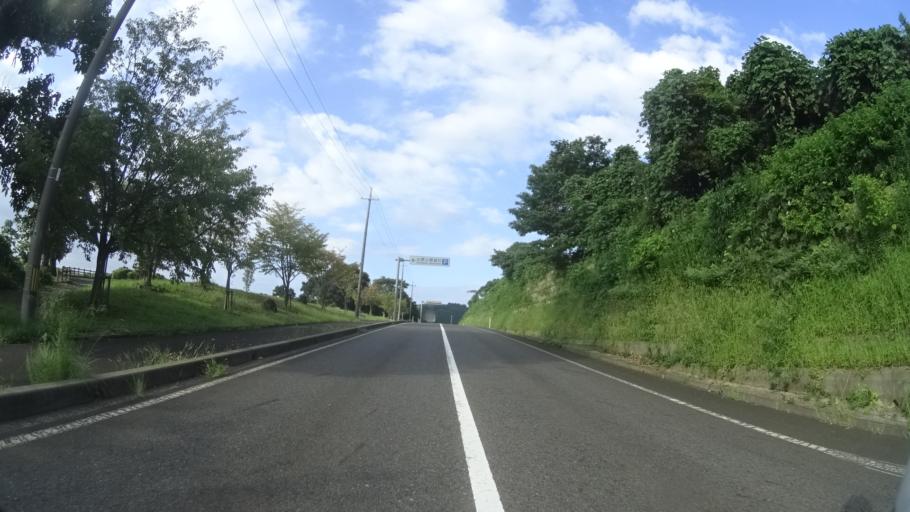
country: JP
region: Tottori
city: Kurayoshi
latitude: 35.4859
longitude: 133.8964
